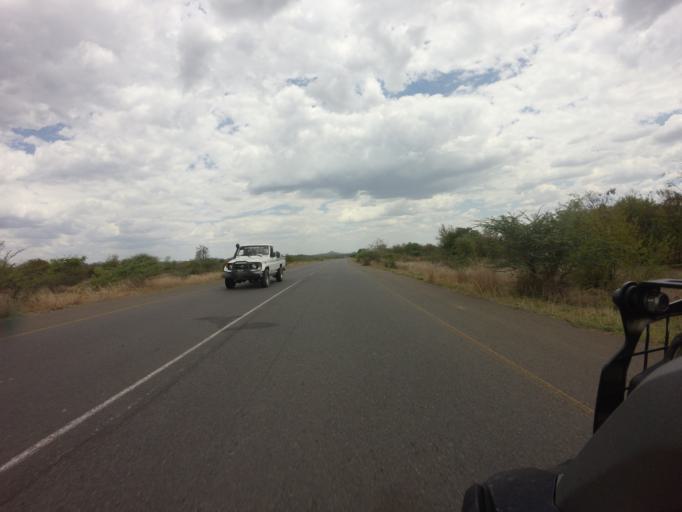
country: AO
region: Huila
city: Lubango
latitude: -15.3300
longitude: 13.8860
